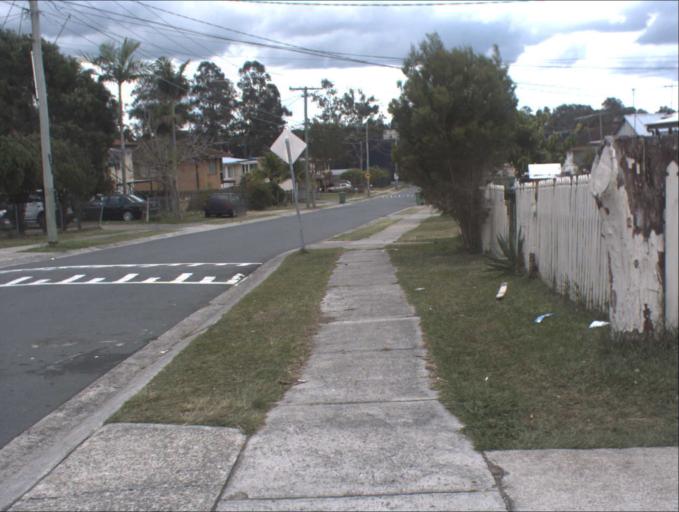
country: AU
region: Queensland
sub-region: Logan
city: Logan City
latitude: -27.6455
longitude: 153.1155
